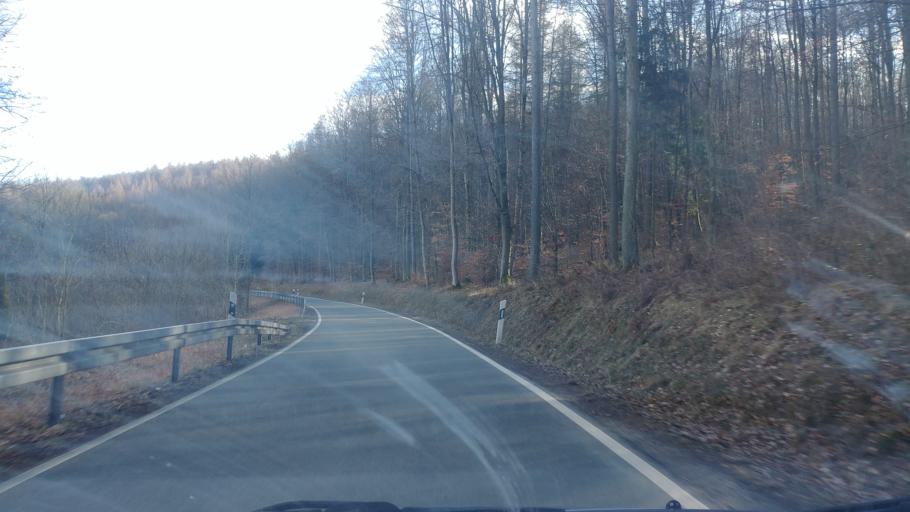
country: DE
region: Lower Saxony
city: Holzminden
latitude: 51.7914
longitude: 9.4728
